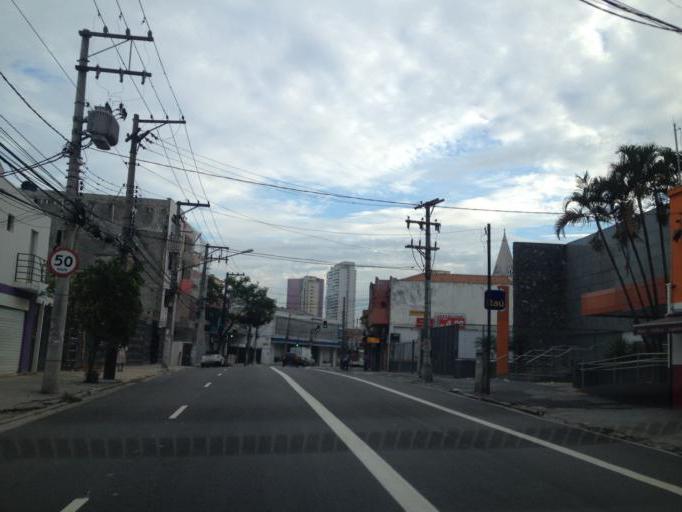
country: BR
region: Sao Paulo
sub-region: Sao Paulo
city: Sao Paulo
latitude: -23.5692
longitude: -46.6973
